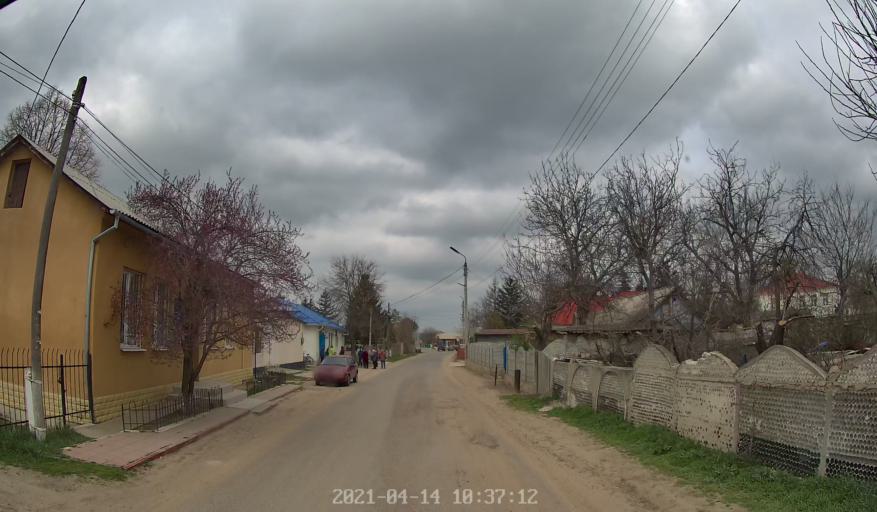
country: MD
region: Criuleni
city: Criuleni
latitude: 47.1468
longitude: 29.1365
